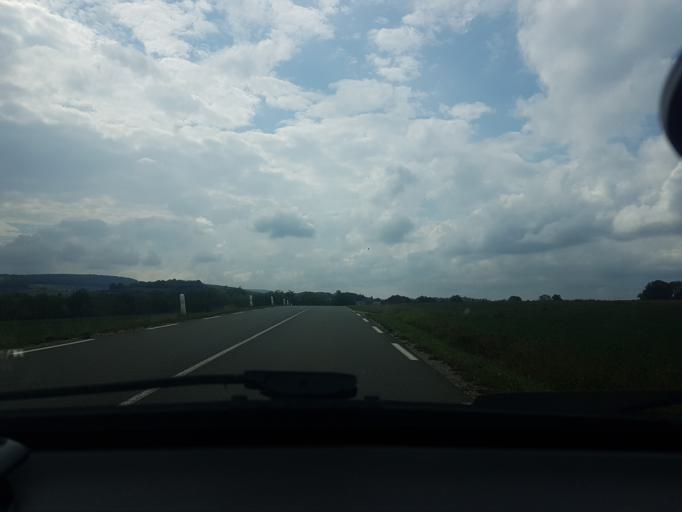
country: FR
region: Franche-Comte
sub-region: Departement du Doubs
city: Arcey
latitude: 47.5646
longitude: 6.6478
